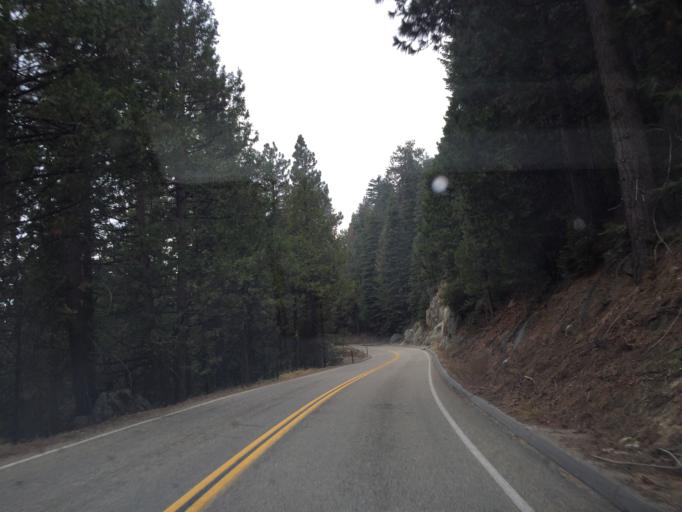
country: US
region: California
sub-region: Tulare County
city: Three Rivers
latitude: 36.7180
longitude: -118.9519
